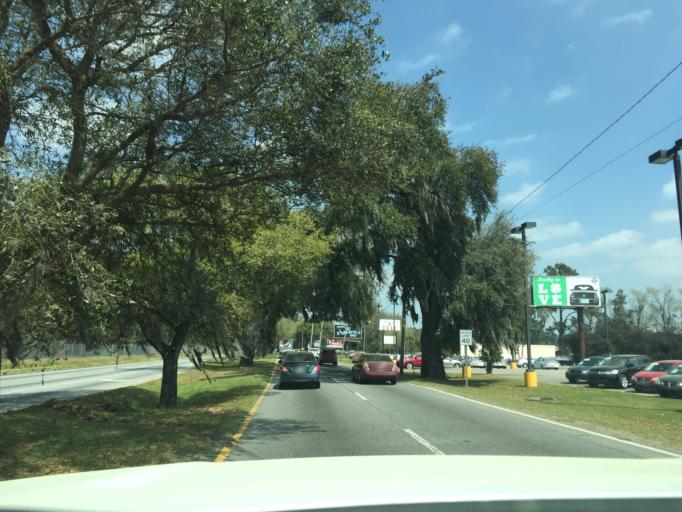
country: US
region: Georgia
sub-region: Chatham County
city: Isle of Hope
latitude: 32.0110
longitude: -81.1169
